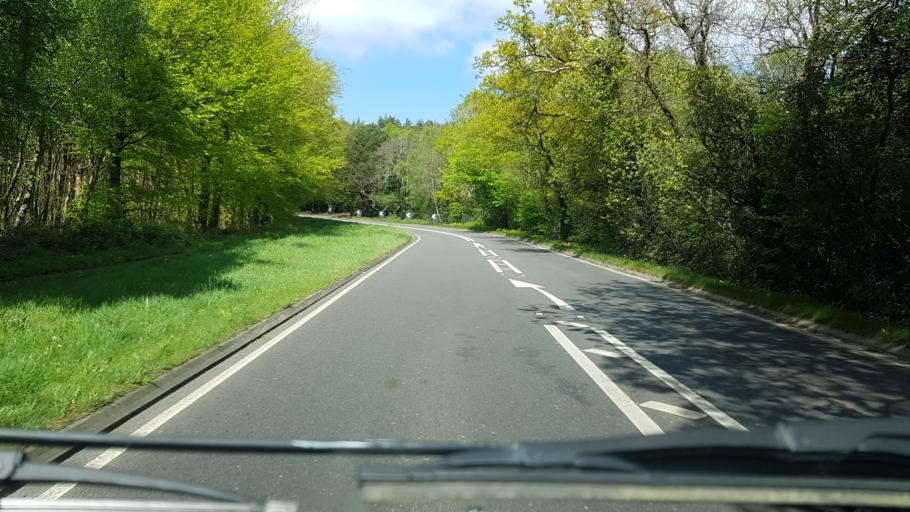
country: GB
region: England
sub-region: Kent
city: Hawkhurst
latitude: 51.0499
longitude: 0.4488
